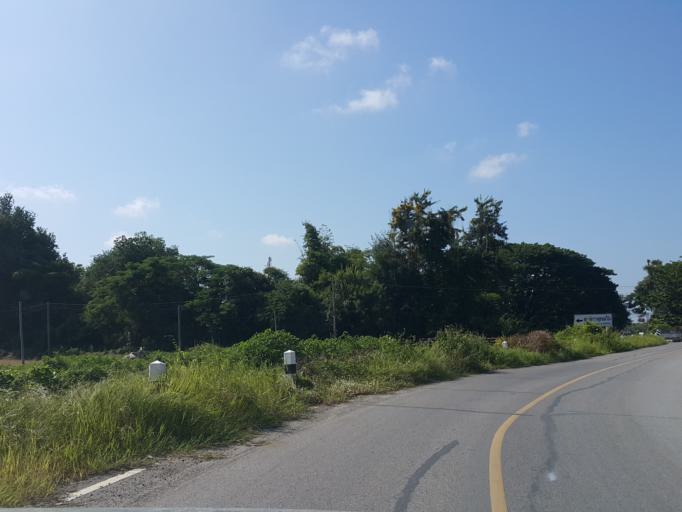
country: TH
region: Chiang Mai
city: Mae On
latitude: 18.8228
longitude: 99.1731
